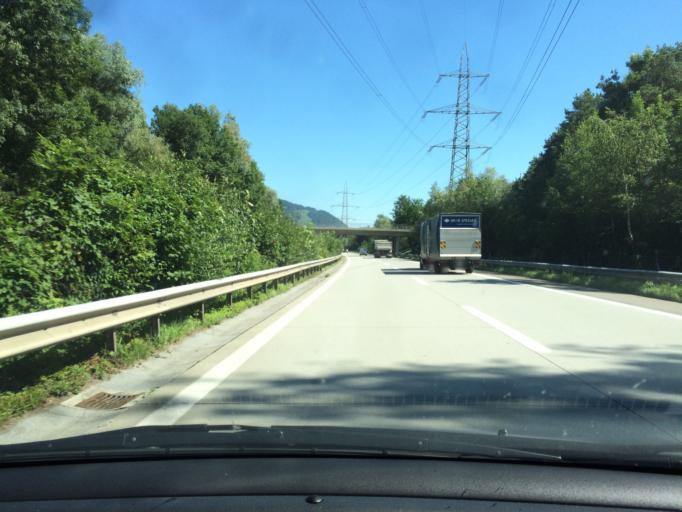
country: LI
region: Ruggell
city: Ruggell
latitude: 47.2605
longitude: 9.5274
